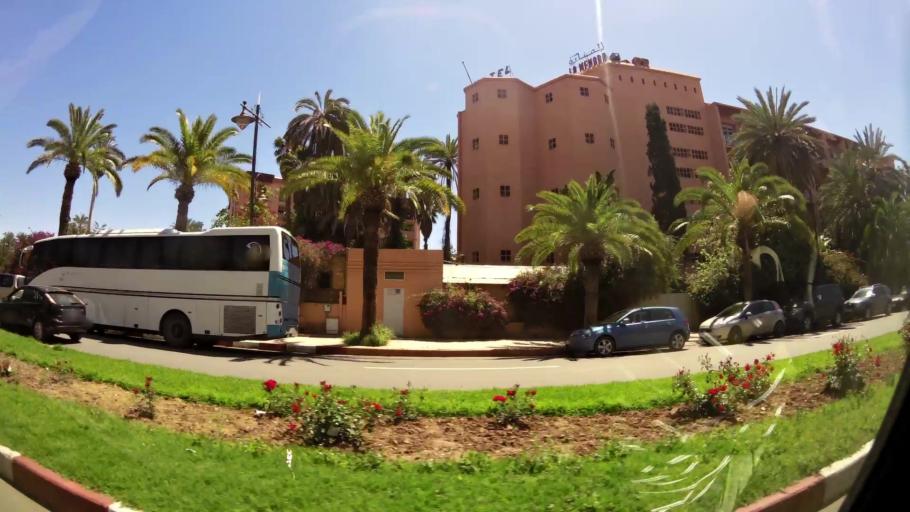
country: MA
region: Marrakech-Tensift-Al Haouz
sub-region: Marrakech
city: Marrakesh
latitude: 31.6284
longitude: -8.0034
